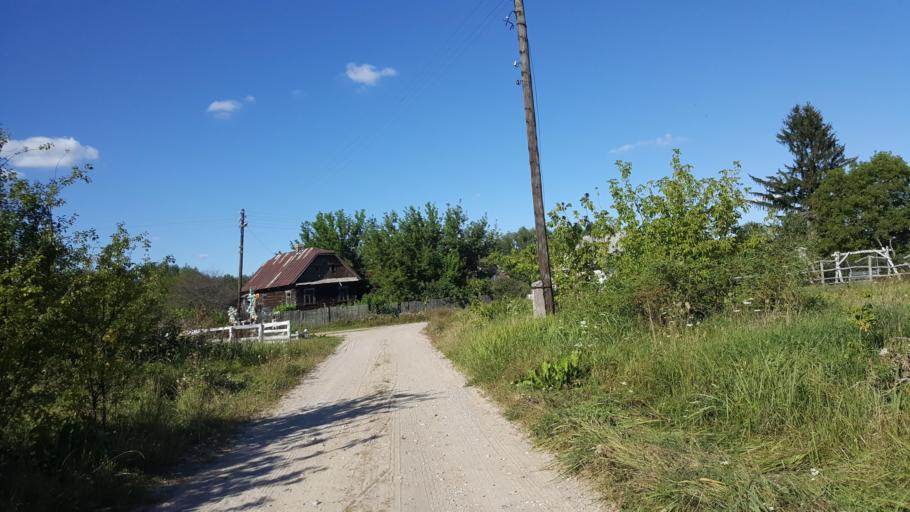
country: BY
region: Brest
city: Vysokaye
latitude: 52.3272
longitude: 23.5511
